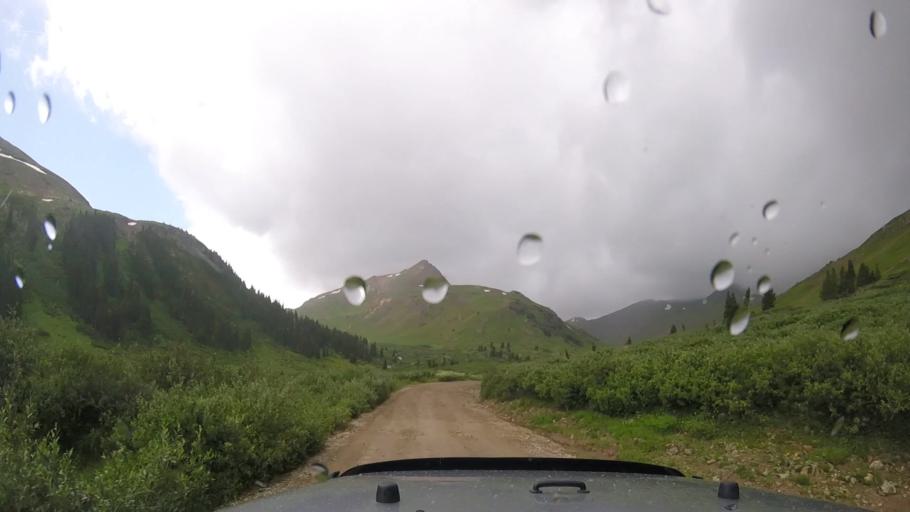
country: US
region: Colorado
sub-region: Ouray County
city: Ouray
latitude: 37.9323
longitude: -107.5829
